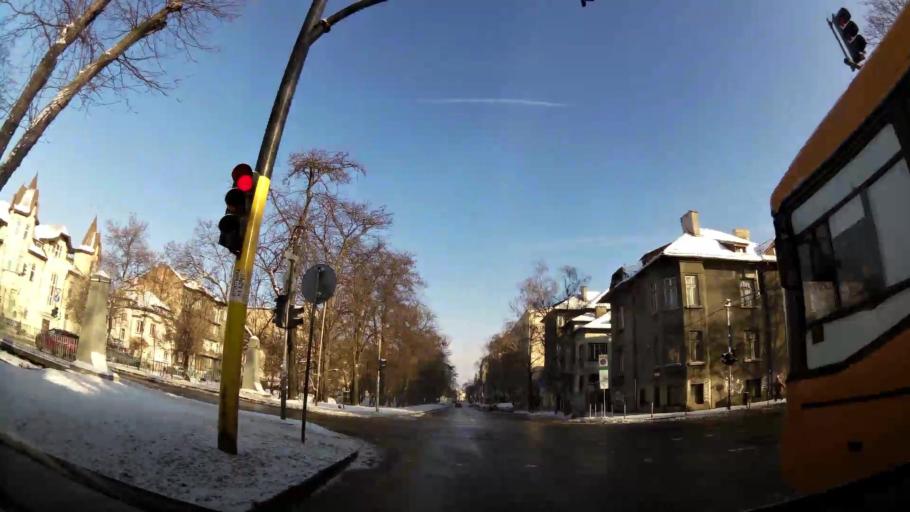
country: BG
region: Sofia-Capital
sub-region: Stolichna Obshtina
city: Sofia
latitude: 42.6940
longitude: 23.3466
